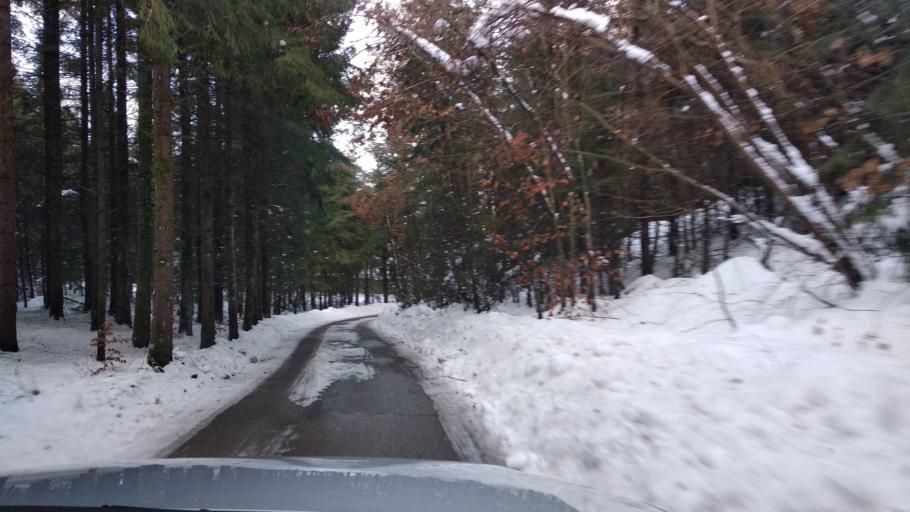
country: DE
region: Bavaria
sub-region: Upper Bavaria
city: Kirchseeon
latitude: 48.0702
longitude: 11.8804
